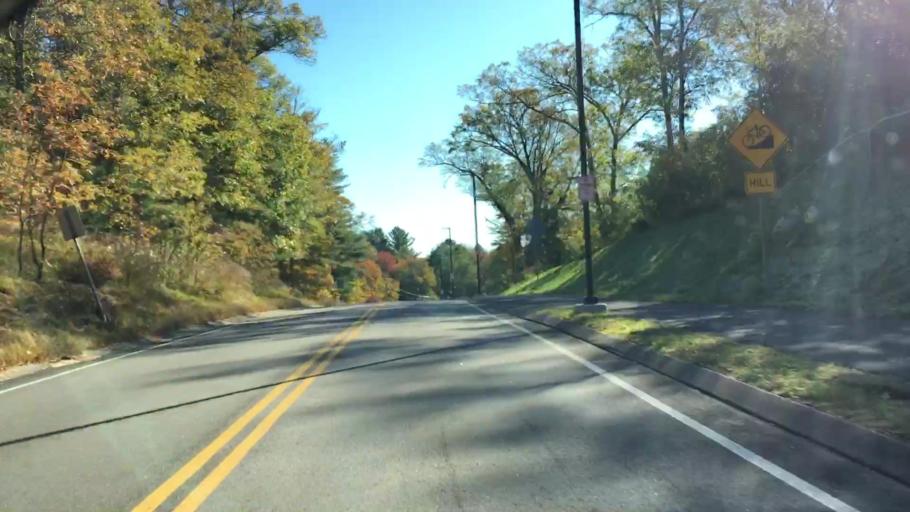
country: US
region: Massachusetts
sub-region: Middlesex County
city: Ashland
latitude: 42.2538
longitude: -71.4722
